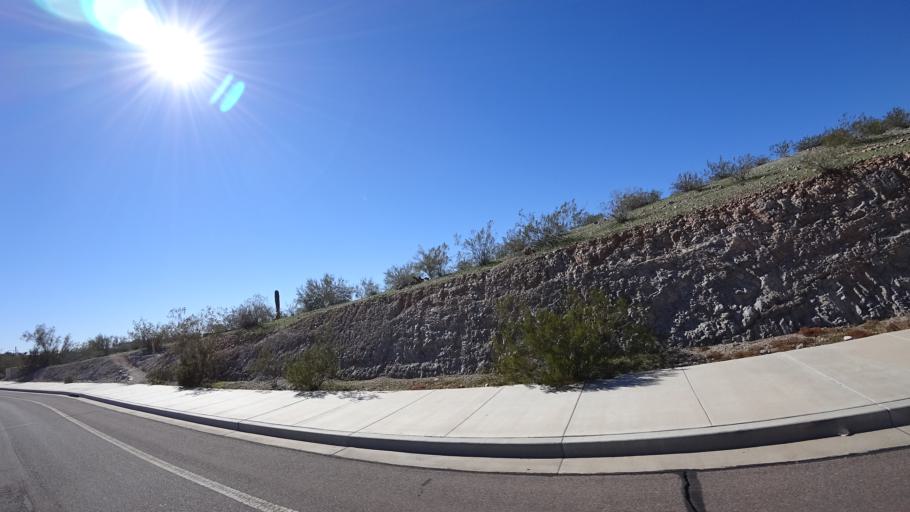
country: US
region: Arizona
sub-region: Maricopa County
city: Goodyear
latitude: 33.3582
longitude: -112.4314
